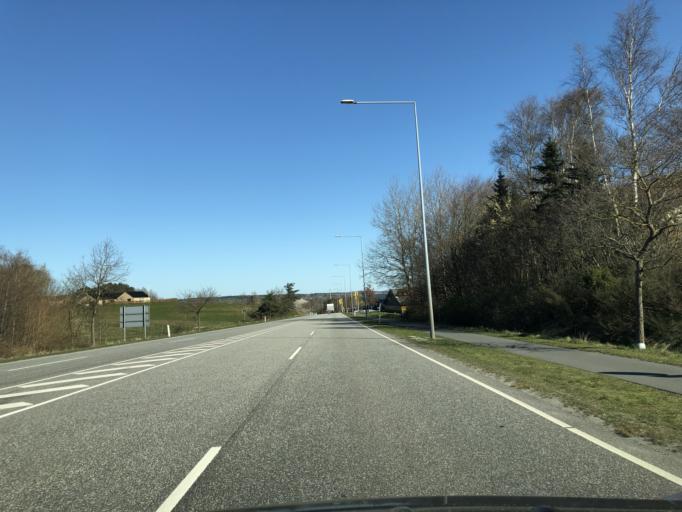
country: DK
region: North Denmark
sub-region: Rebild Kommune
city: Stovring
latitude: 56.8728
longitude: 9.8385
